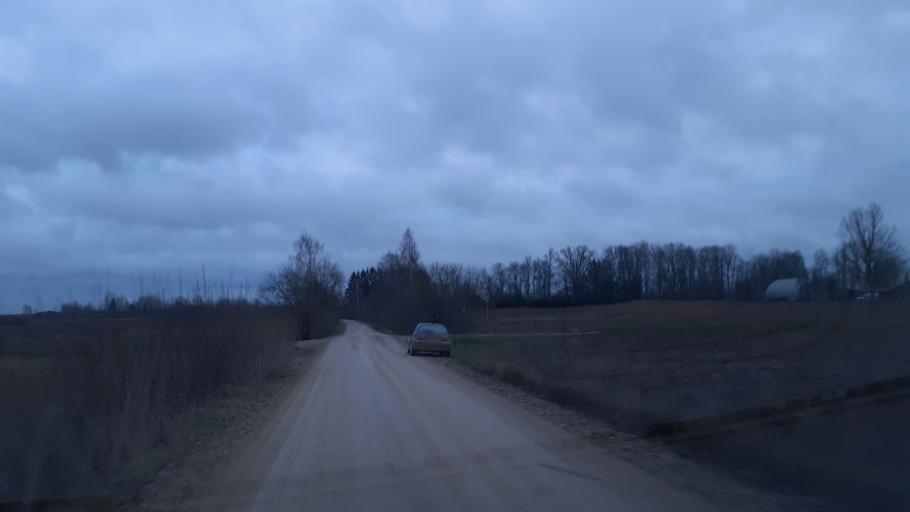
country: LV
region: Kuldigas Rajons
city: Kuldiga
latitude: 57.0466
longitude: 22.1312
